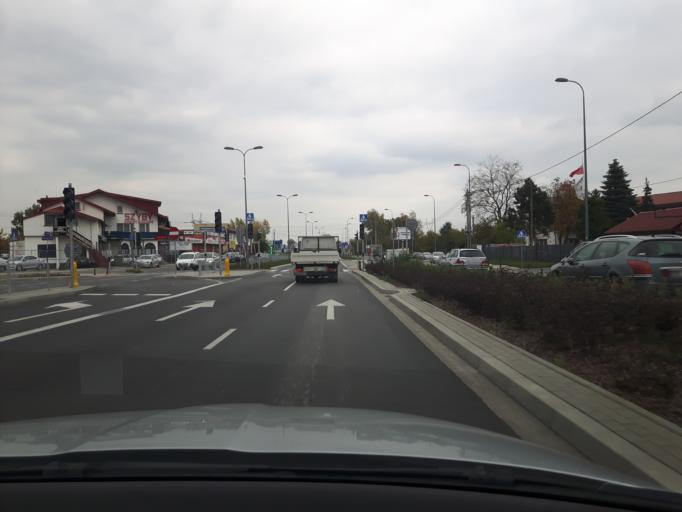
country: PL
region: Masovian Voivodeship
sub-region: Powiat wolominski
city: Zabki
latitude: 52.2864
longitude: 21.0882
